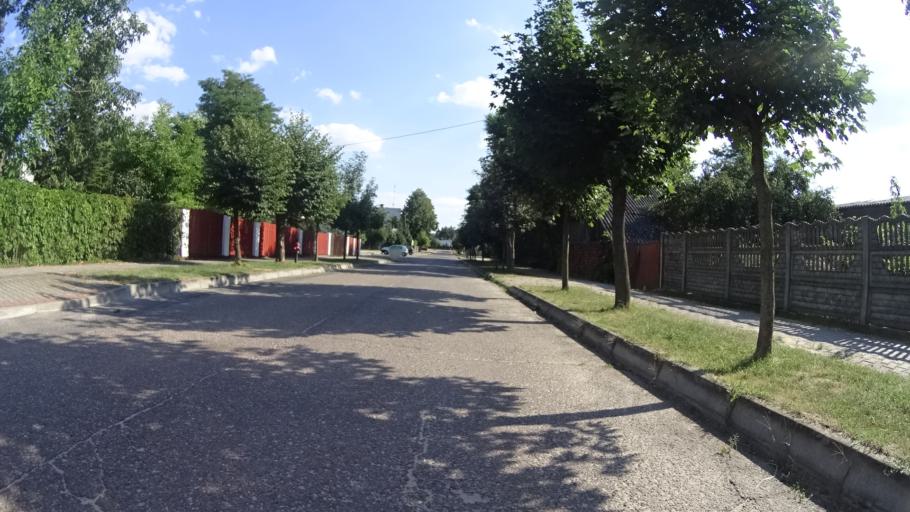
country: PL
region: Masovian Voivodeship
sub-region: Powiat bialobrzeski
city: Wysmierzyce
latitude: 51.6269
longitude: 20.8224
